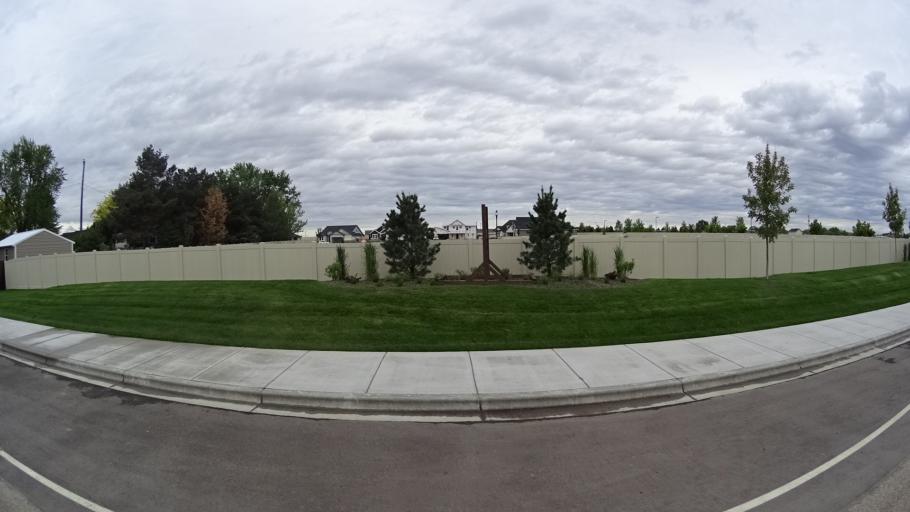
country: US
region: Idaho
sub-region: Ada County
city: Star
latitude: 43.7121
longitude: -116.4683
